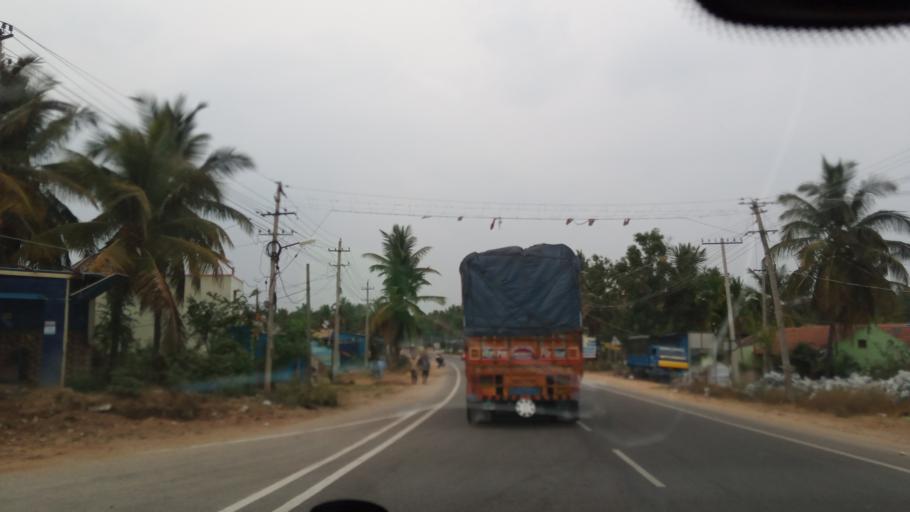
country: IN
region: Karnataka
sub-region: Mandya
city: Nagamangala
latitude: 12.8078
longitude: 76.7538
